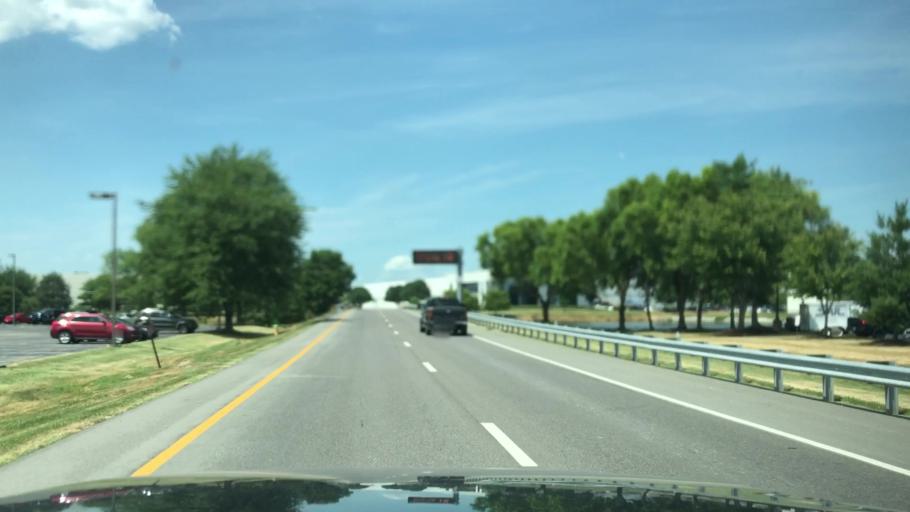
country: US
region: Missouri
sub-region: Saint Charles County
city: Saint Charles
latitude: 38.7678
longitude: -90.4566
